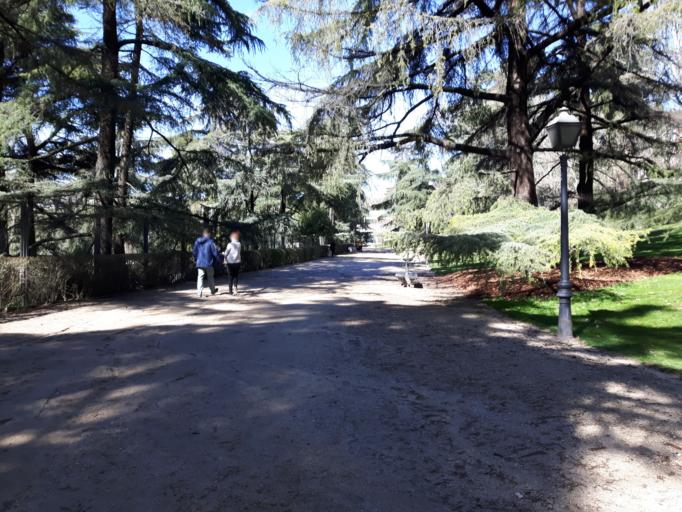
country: ES
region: Madrid
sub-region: Provincia de Madrid
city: Moncloa-Aravaca
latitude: 40.4264
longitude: -3.7204
